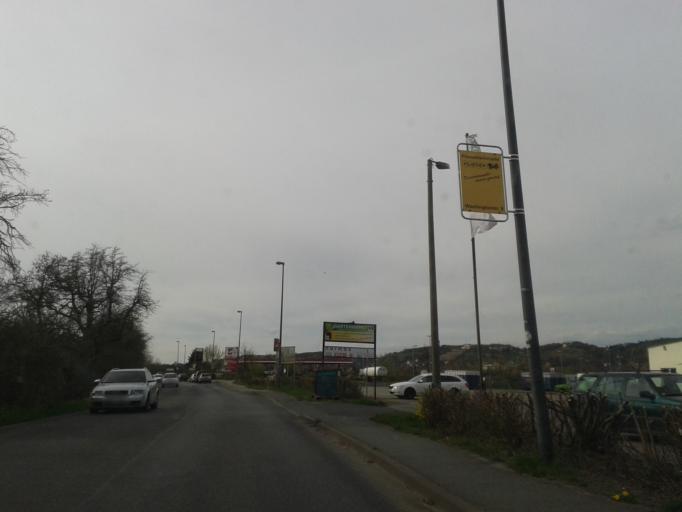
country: DE
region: Saxony
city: Radebeul
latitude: 51.0971
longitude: 13.6550
